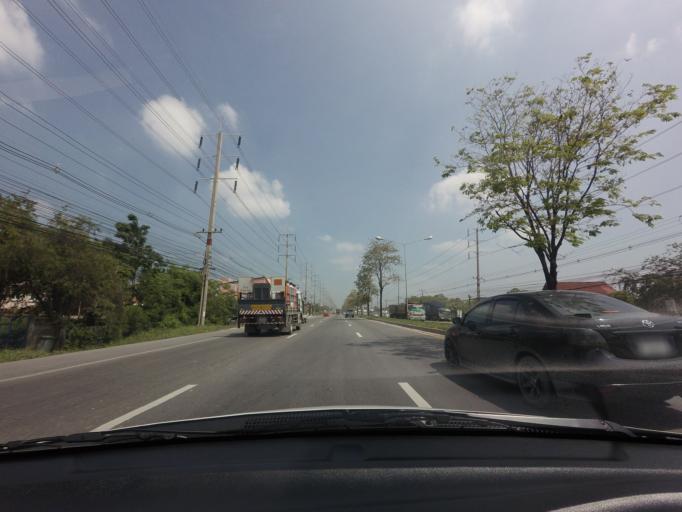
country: TH
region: Chachoengsao
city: Bang Pakong
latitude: 13.5807
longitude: 101.0073
